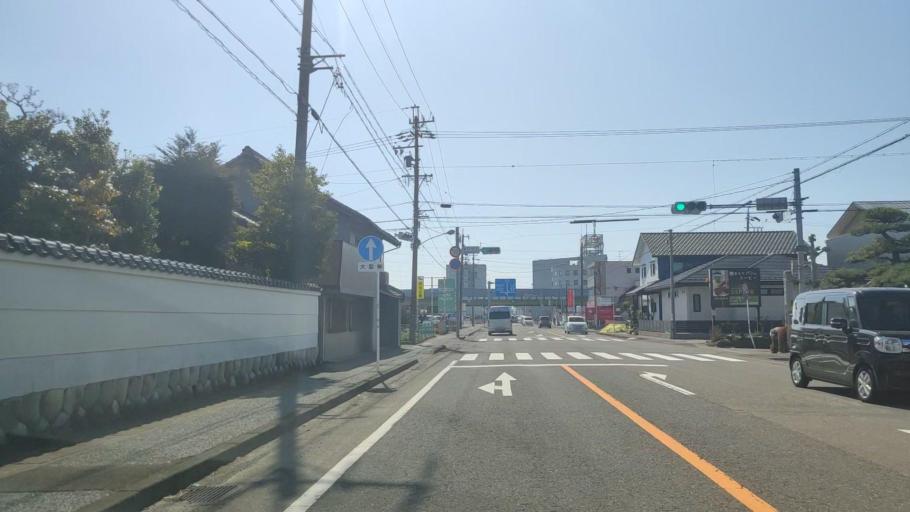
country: JP
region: Gifu
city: Kasamatsucho
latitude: 35.3896
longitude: 136.7641
